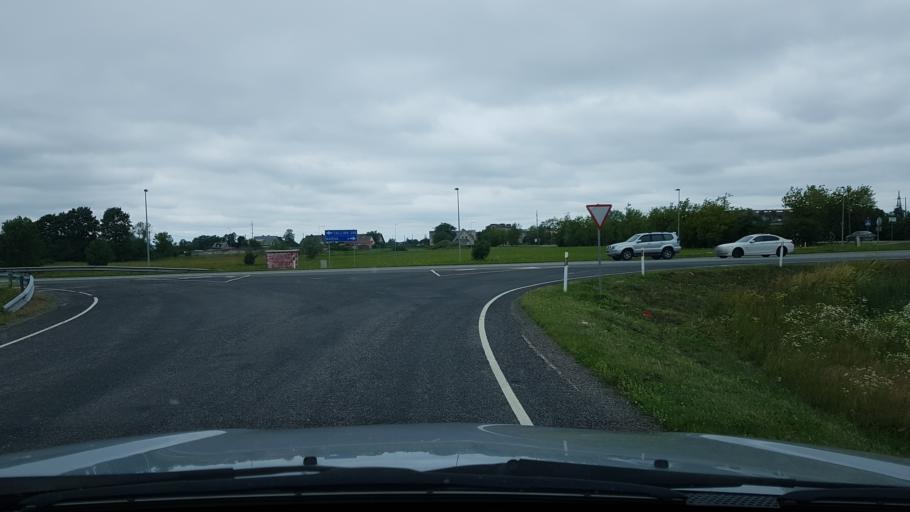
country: EE
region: Ida-Virumaa
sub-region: Narva linn
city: Narva
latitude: 59.3883
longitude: 28.1301
